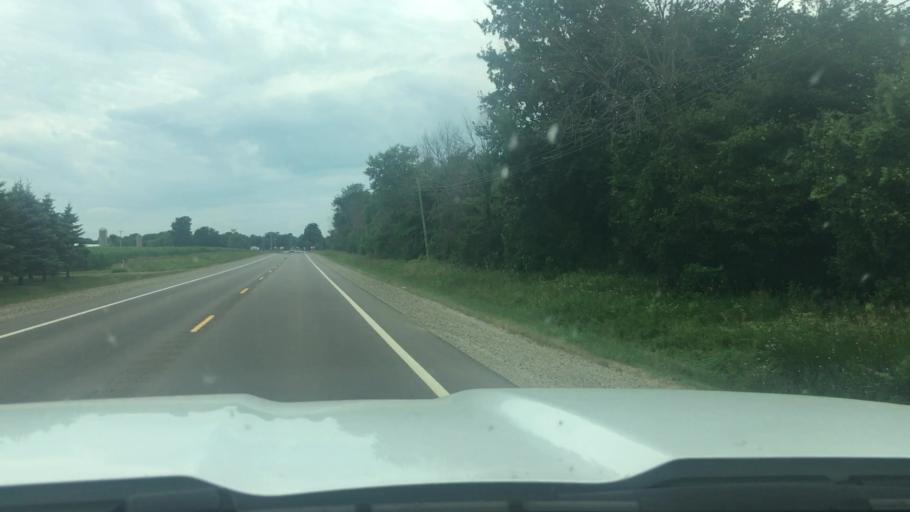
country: US
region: Michigan
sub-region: Clinton County
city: Fowler
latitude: 43.0018
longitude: -84.8277
